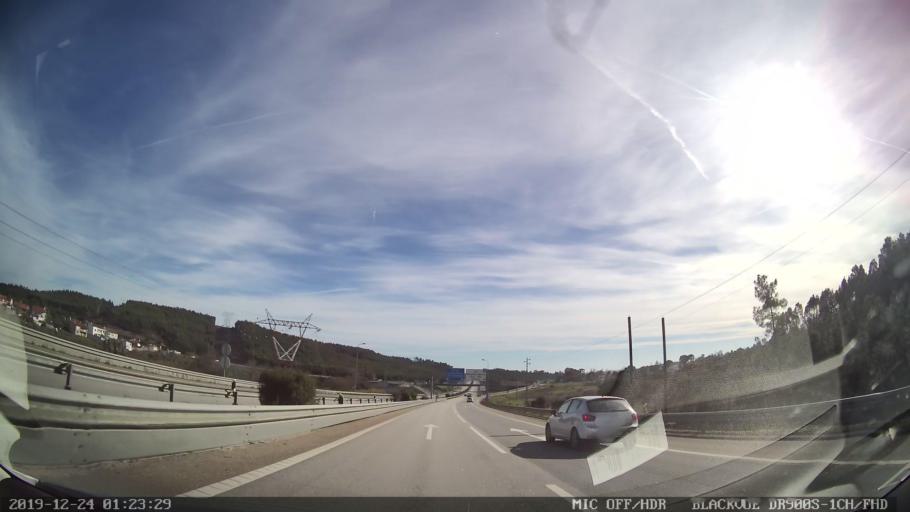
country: PT
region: Santarem
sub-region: Abrantes
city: Alferrarede
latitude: 39.4937
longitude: -8.1813
